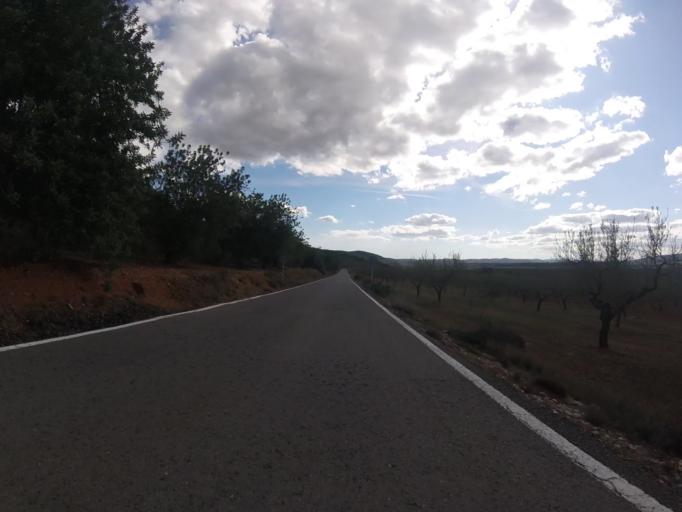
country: ES
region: Valencia
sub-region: Provincia de Castello
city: Cuevas de Vinroma
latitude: 40.3623
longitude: 0.1237
